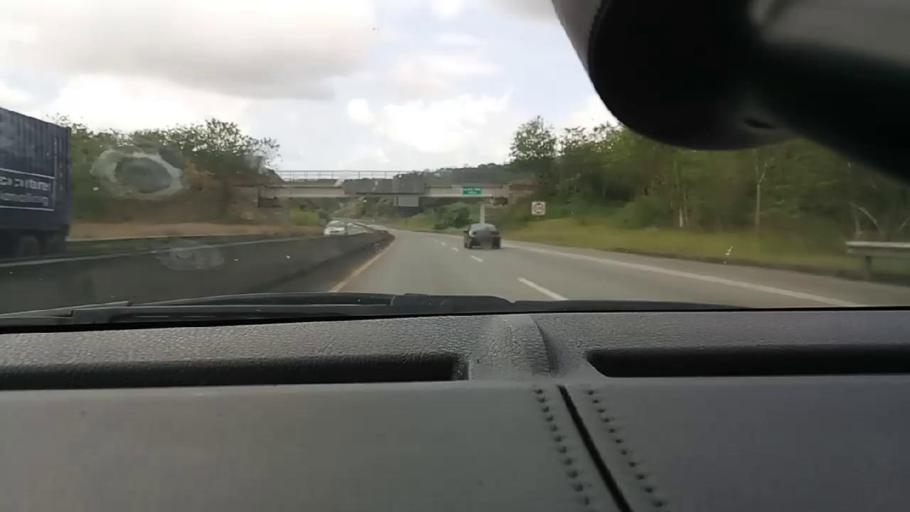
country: PA
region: Colon
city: Gatun
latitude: 9.2839
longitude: -79.7438
